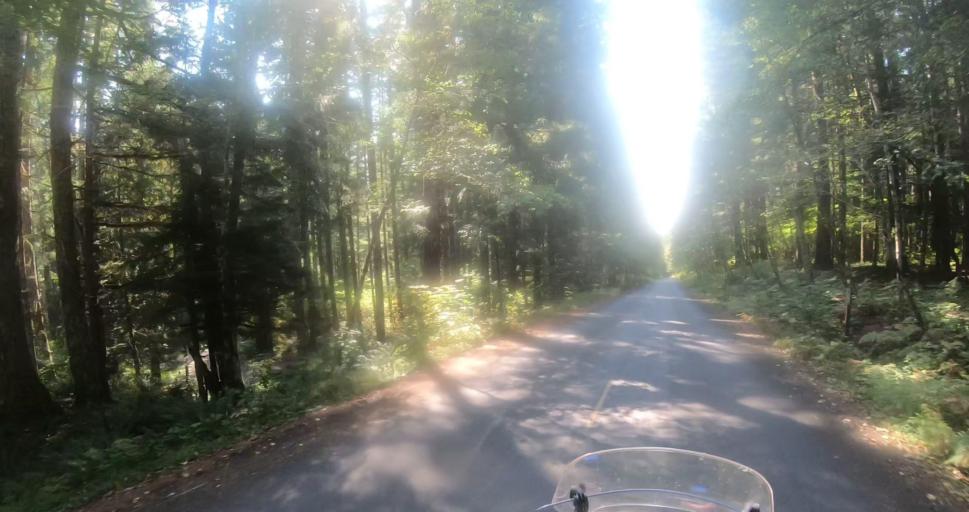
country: US
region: Washington
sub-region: Skamania County
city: Carson
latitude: 46.1580
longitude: -121.8814
